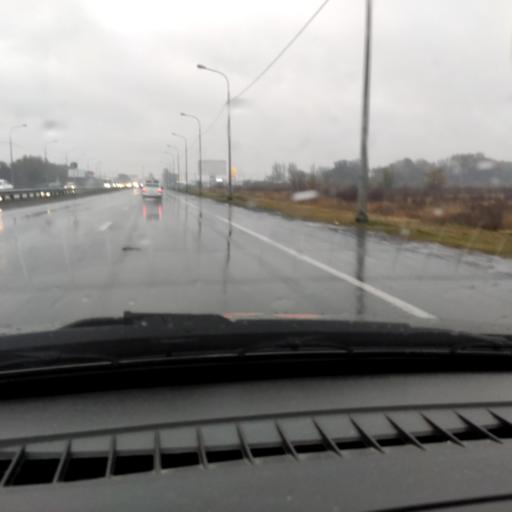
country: RU
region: Samara
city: Tol'yatti
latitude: 53.5733
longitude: 49.4551
